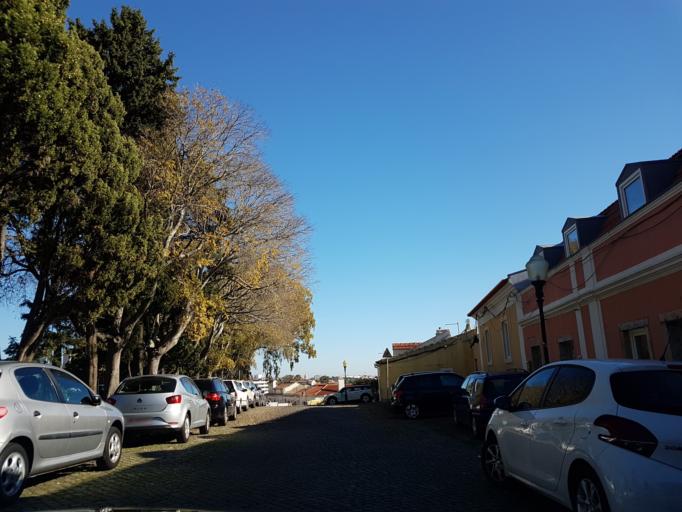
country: PT
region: Lisbon
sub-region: Oeiras
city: Alges
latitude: 38.7072
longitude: -9.1965
